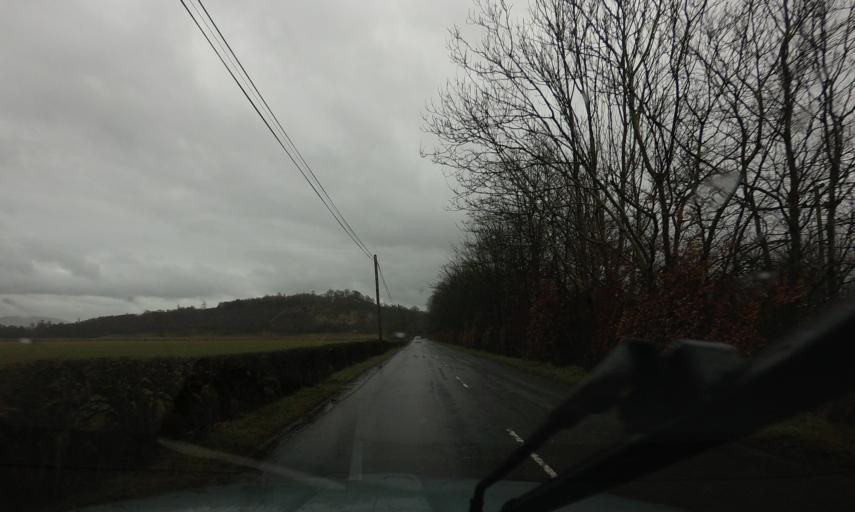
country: GB
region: Scotland
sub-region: Stirling
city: Balfron
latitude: 56.1499
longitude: -4.3608
